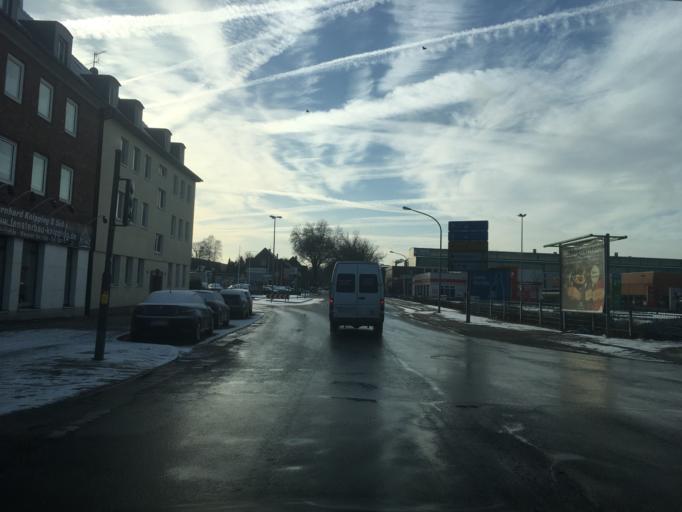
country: DE
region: North Rhine-Westphalia
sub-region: Regierungsbezirk Dusseldorf
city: Oberhausen
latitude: 51.5165
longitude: 6.8565
